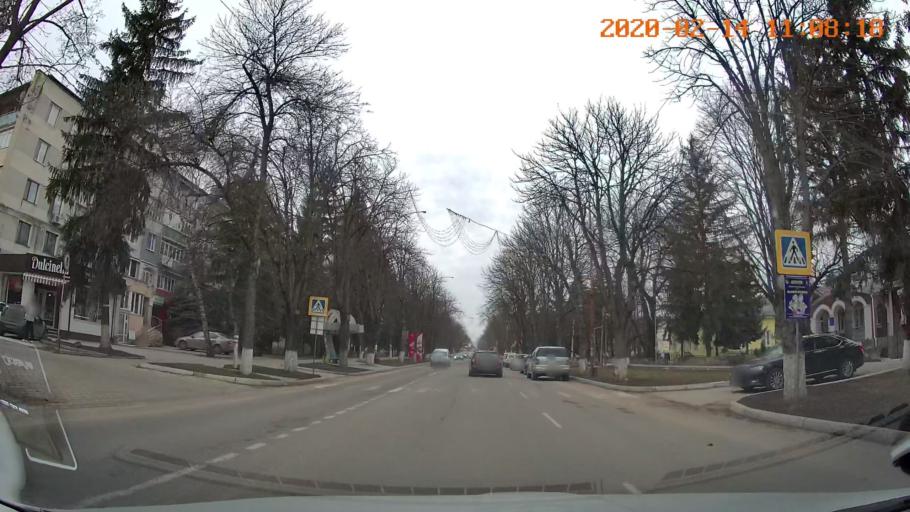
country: MD
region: Raionul Edinet
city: Edinet
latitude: 48.1714
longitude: 27.3032
